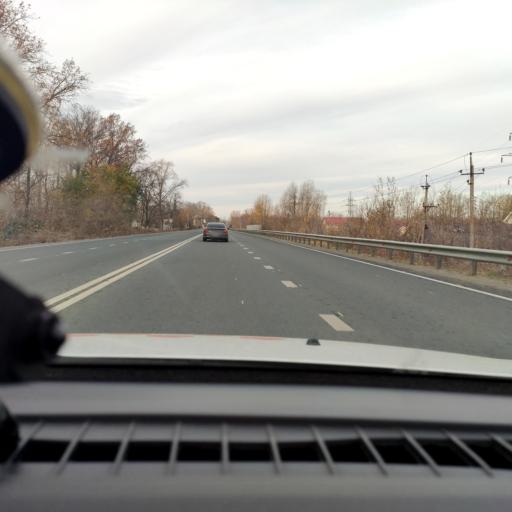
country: RU
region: Samara
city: Novokuybyshevsk
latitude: 53.1444
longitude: 49.9993
